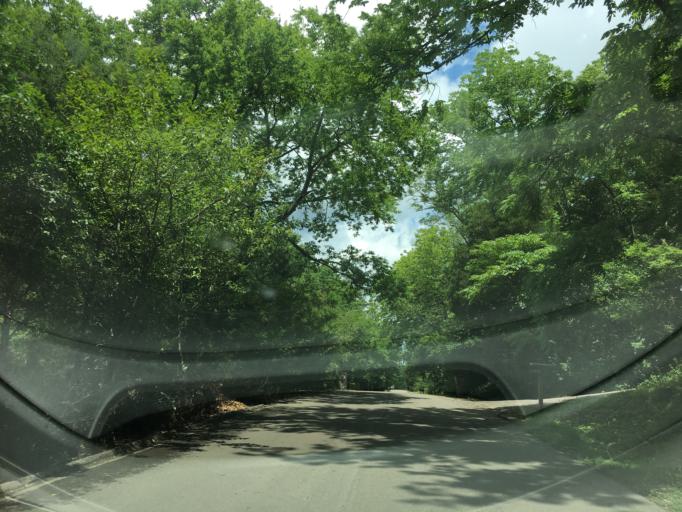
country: US
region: Tennessee
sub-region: Davidson County
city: Belle Meade
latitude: 36.0874
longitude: -86.8494
